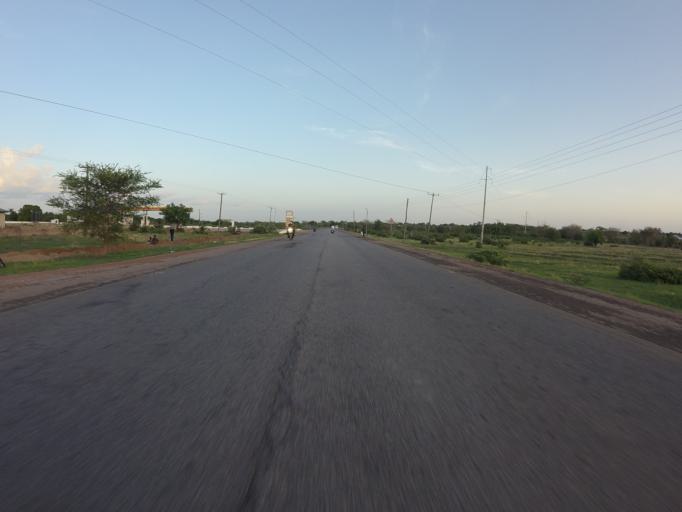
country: GH
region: Upper East
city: Navrongo
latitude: 10.9350
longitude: -1.0897
